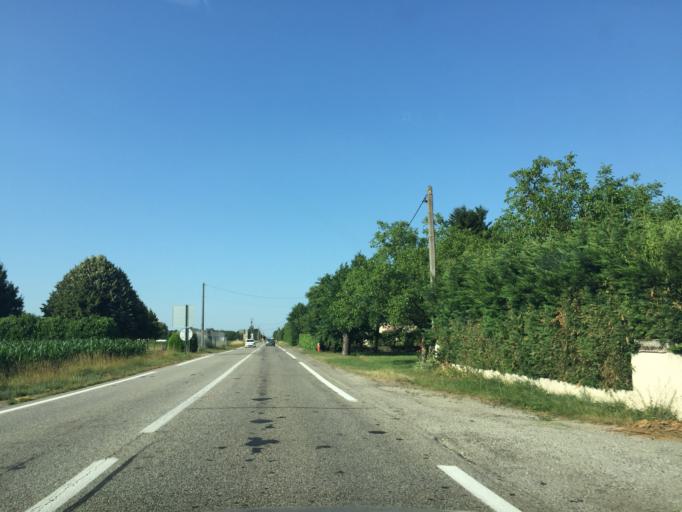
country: FR
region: Rhone-Alpes
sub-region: Departement de l'Isere
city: Saint-Just-de-Claix
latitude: 45.0777
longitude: 5.2864
